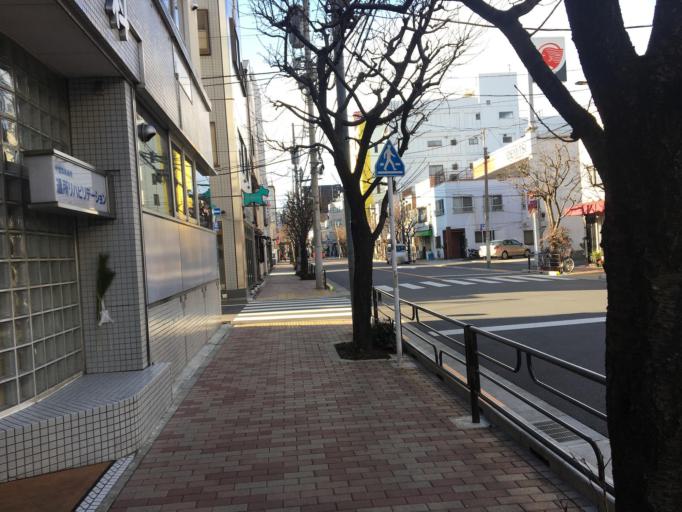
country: JP
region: Saitama
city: Soka
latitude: 35.7196
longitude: 139.7967
